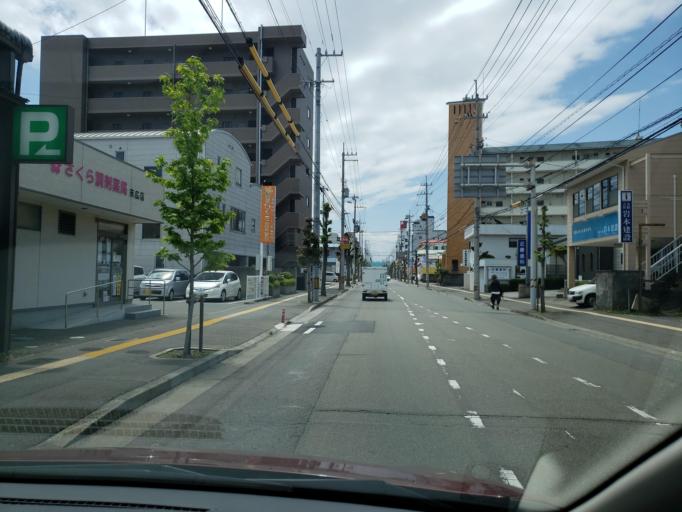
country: JP
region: Tokushima
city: Tokushima-shi
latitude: 34.0657
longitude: 134.5719
